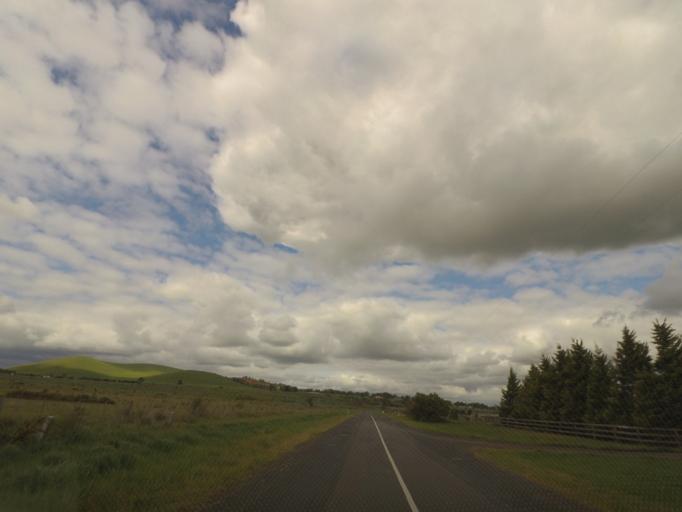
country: AU
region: Victoria
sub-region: Hume
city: Craigieburn
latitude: -37.4679
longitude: 144.9615
